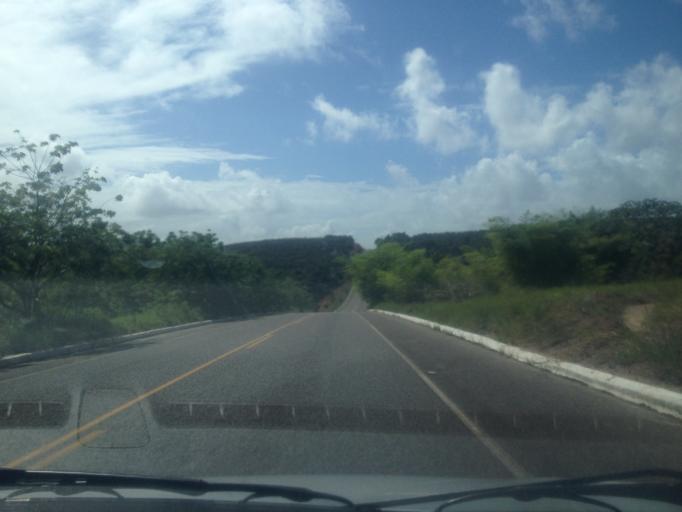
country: BR
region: Bahia
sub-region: Conde
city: Conde
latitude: -11.9184
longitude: -37.6632
